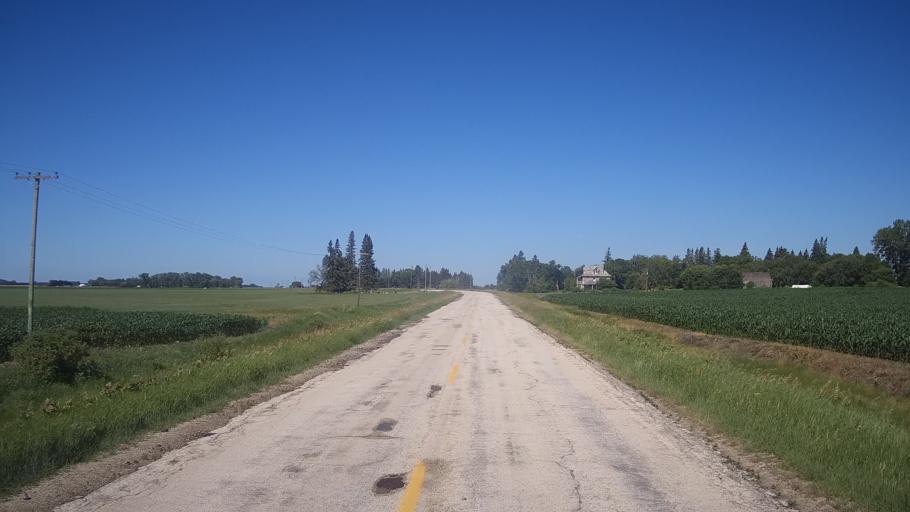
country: CA
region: Manitoba
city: Portage la Prairie
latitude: 50.0437
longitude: -98.0530
